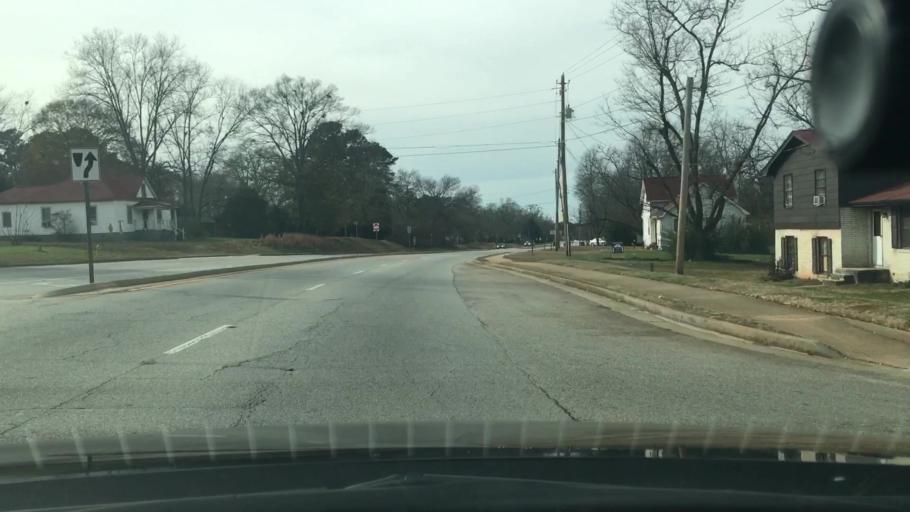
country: US
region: Georgia
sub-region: Spalding County
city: Experiment
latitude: 33.2735
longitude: -84.2989
